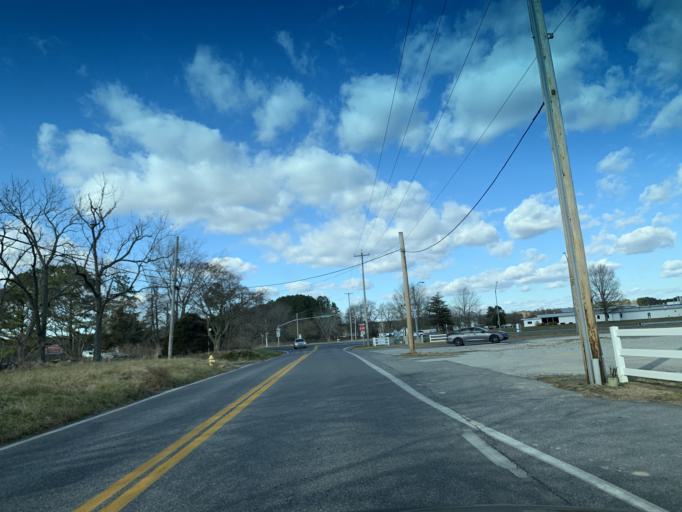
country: US
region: Maryland
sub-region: Worcester County
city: Berlin
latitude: 38.3425
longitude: -75.2195
